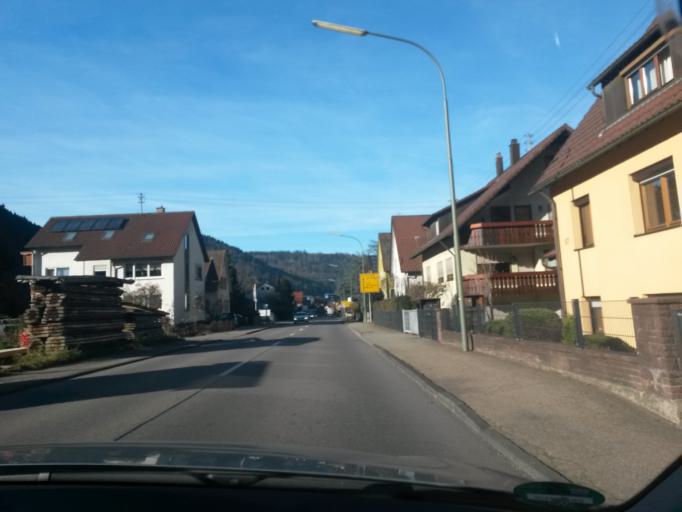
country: DE
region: Baden-Wuerttemberg
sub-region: Karlsruhe Region
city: Hofen an der Enz
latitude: 48.7690
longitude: 8.5857
